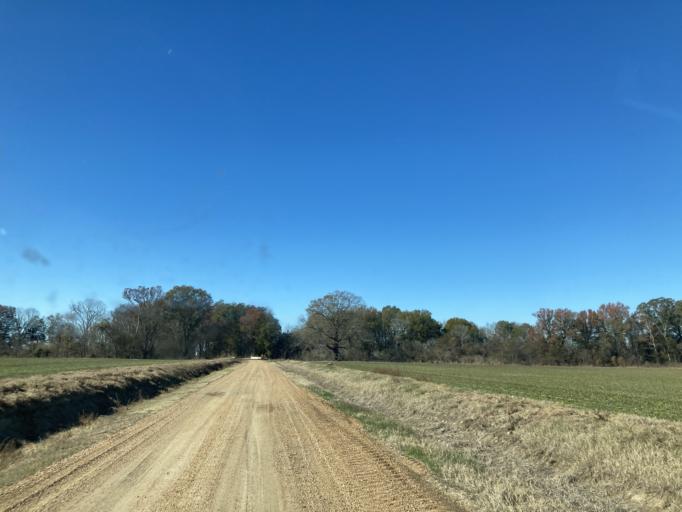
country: US
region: Mississippi
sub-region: Sharkey County
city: Rolling Fork
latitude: 32.8498
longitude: -90.6938
